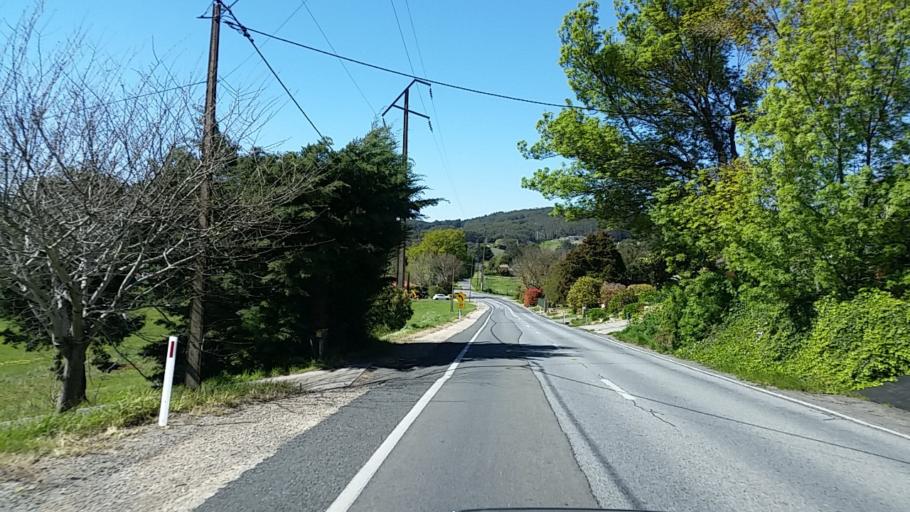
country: AU
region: South Australia
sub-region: Adelaide Hills
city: Bridgewater
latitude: -34.9803
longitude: 138.7284
